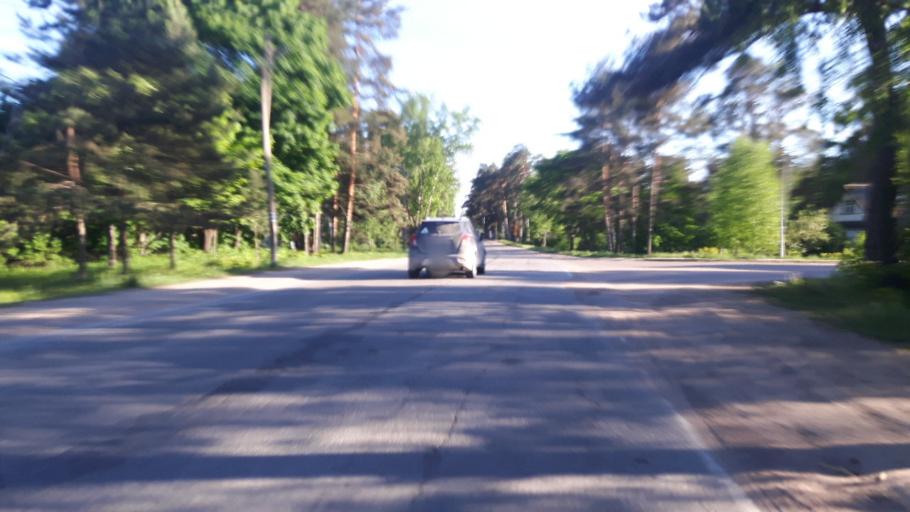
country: RU
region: Leningrad
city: Vistino
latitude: 59.7733
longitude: 28.4756
